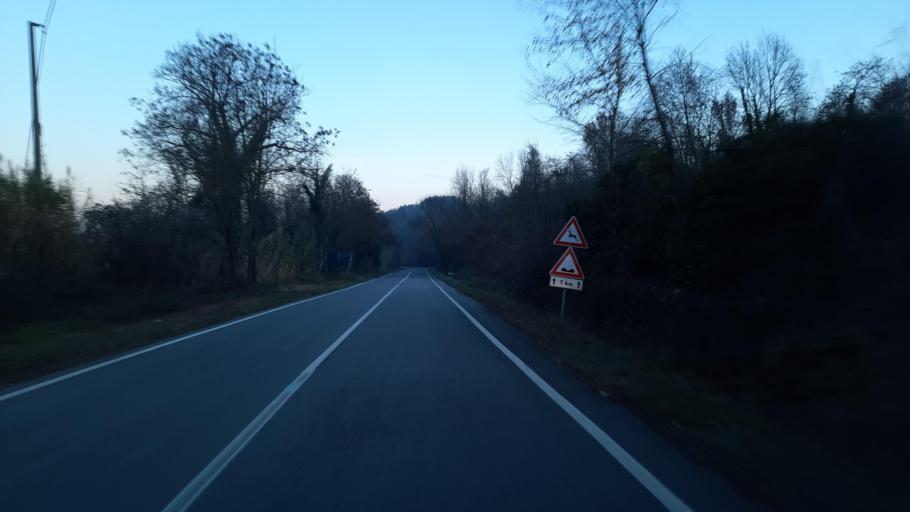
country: IT
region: Piedmont
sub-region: Provincia di Alessandria
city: Camino
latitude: 45.1732
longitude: 8.2812
